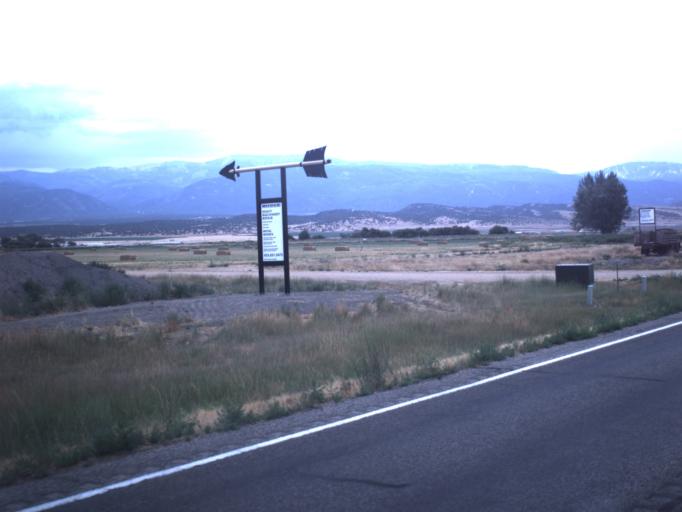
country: US
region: Utah
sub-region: Sanpete County
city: Moroni
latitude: 39.4848
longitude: -111.5630
